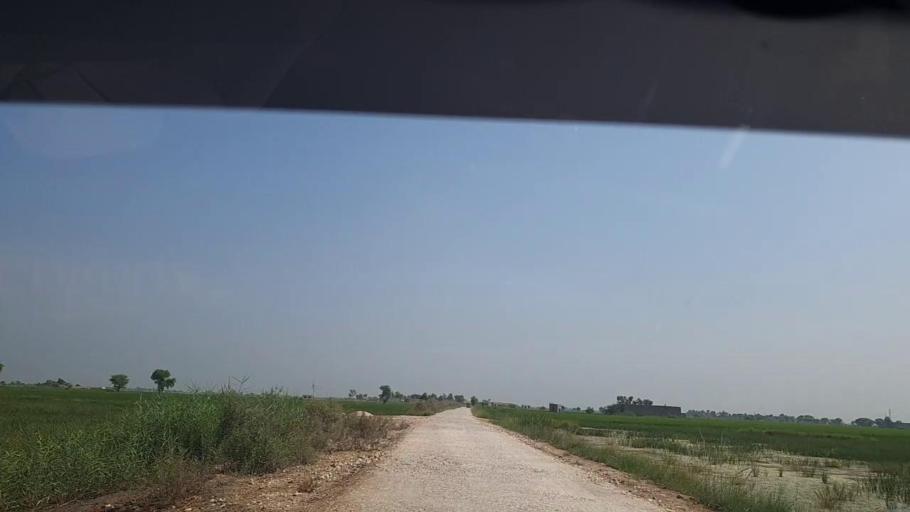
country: PK
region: Sindh
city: Thul
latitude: 28.1987
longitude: 68.7310
